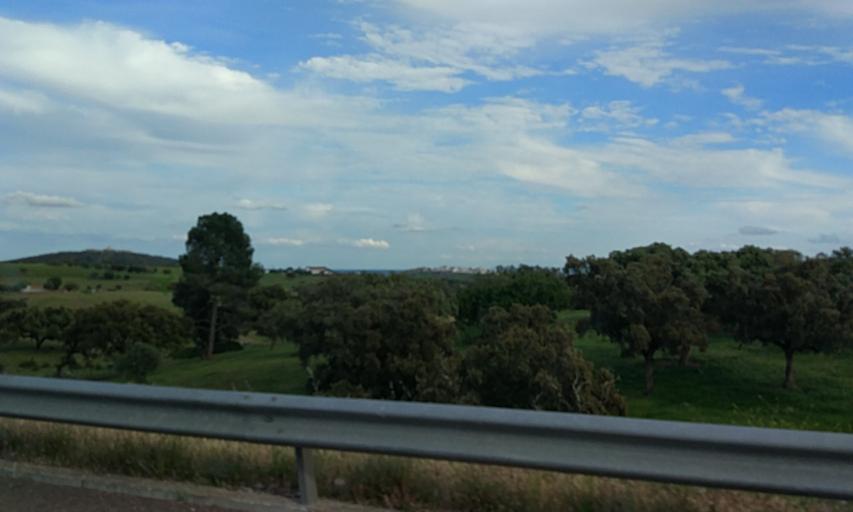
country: PT
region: Portalegre
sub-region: Elvas
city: Elvas
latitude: 38.9003
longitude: -7.1997
